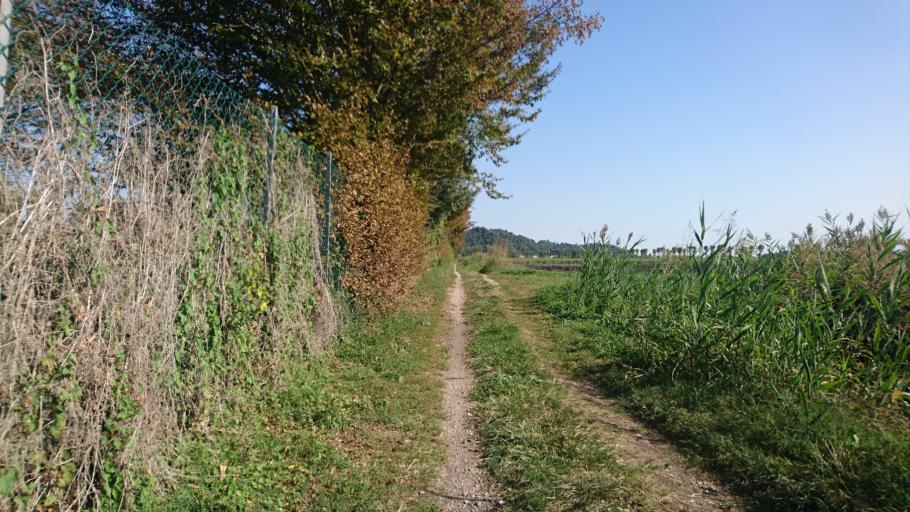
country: IT
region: Veneto
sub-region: Provincia di Padova
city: Galzignano
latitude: 45.2919
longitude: 11.7447
